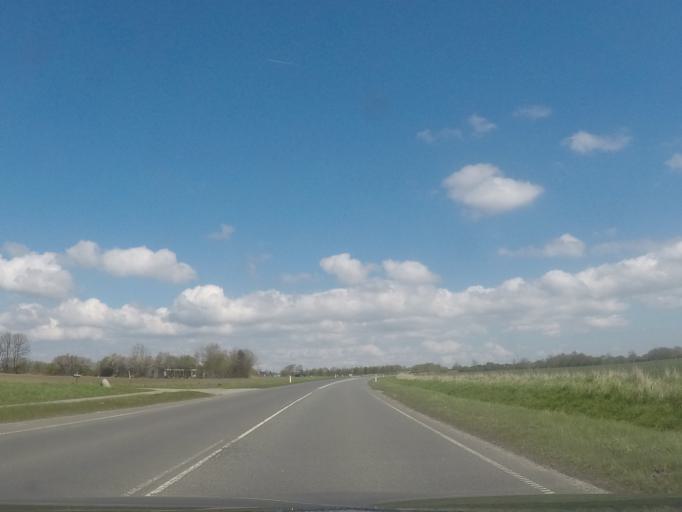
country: DK
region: South Denmark
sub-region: Assens Kommune
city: Vissenbjerg
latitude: 55.3939
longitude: 10.1456
